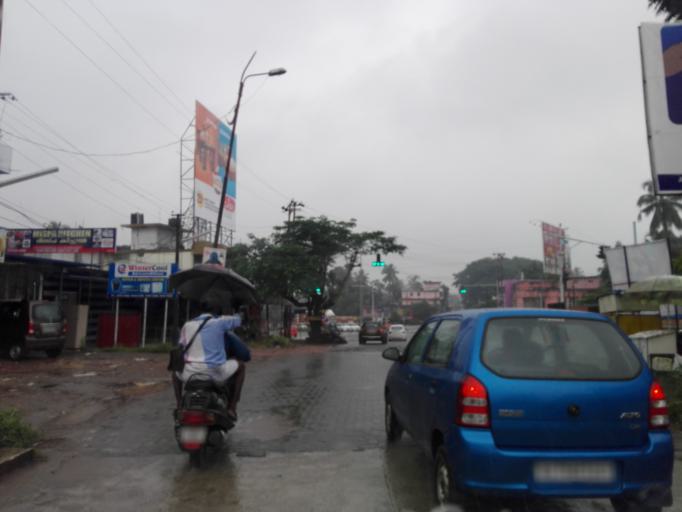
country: IN
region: Kerala
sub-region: Ernakulam
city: Elur
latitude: 10.0669
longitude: 76.3224
